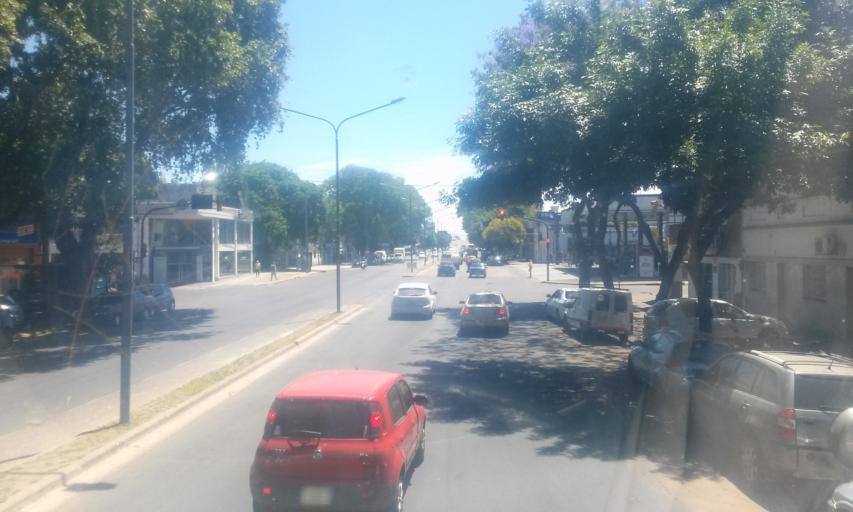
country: AR
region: Santa Fe
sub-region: Departamento de Rosario
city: Rosario
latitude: -32.9395
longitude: -60.6793
